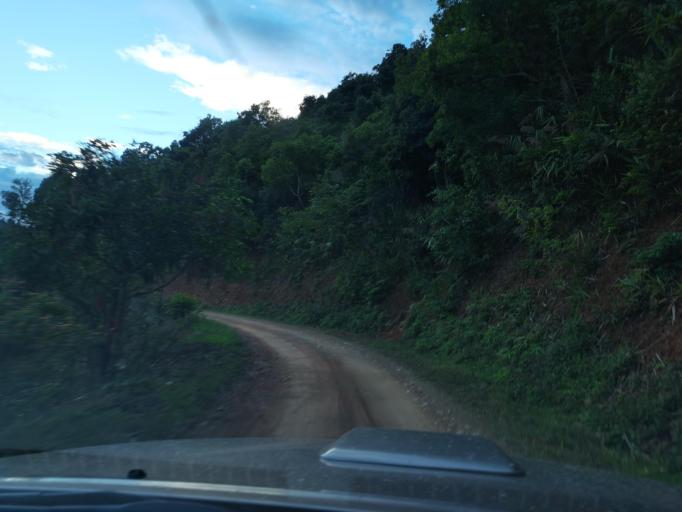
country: LA
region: Phongsali
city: Phongsali
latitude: 21.6491
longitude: 102.1294
